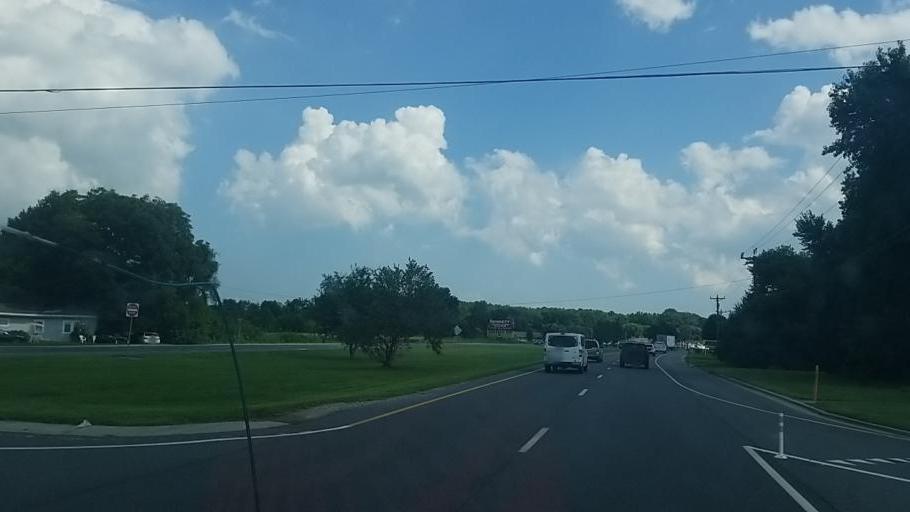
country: US
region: Delaware
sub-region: Sussex County
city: Selbyville
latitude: 38.5174
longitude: -75.2403
